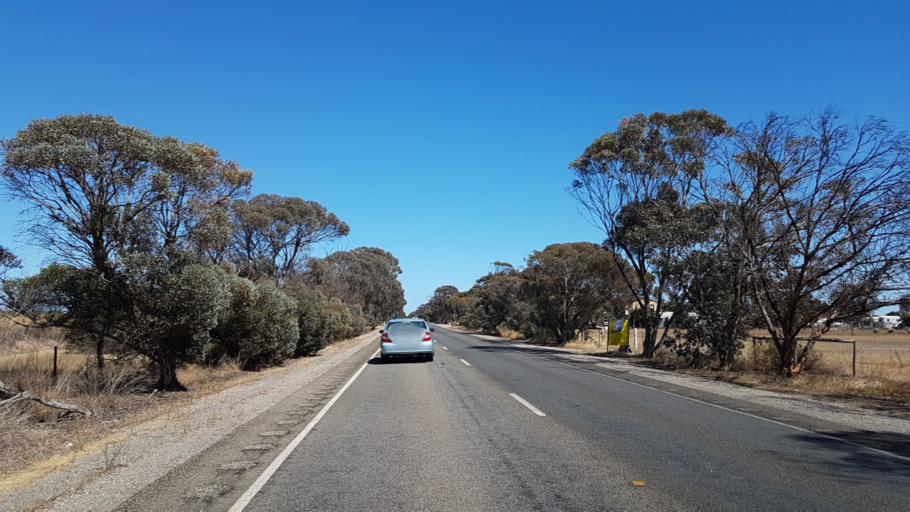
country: AU
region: South Australia
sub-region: Copper Coast
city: Kadina
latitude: -33.9710
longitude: 137.7387
